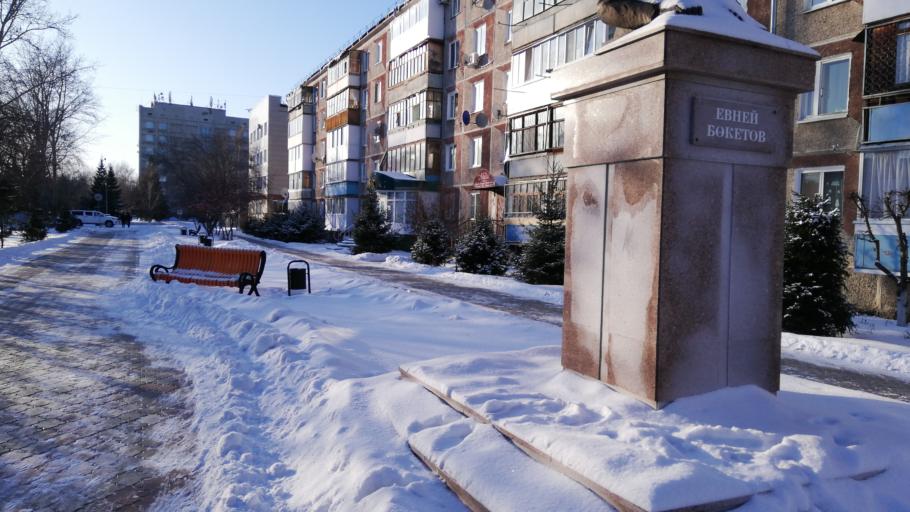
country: KZ
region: Soltustik Qazaqstan
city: Petropavlovsk
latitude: 54.8638
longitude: 69.1447
